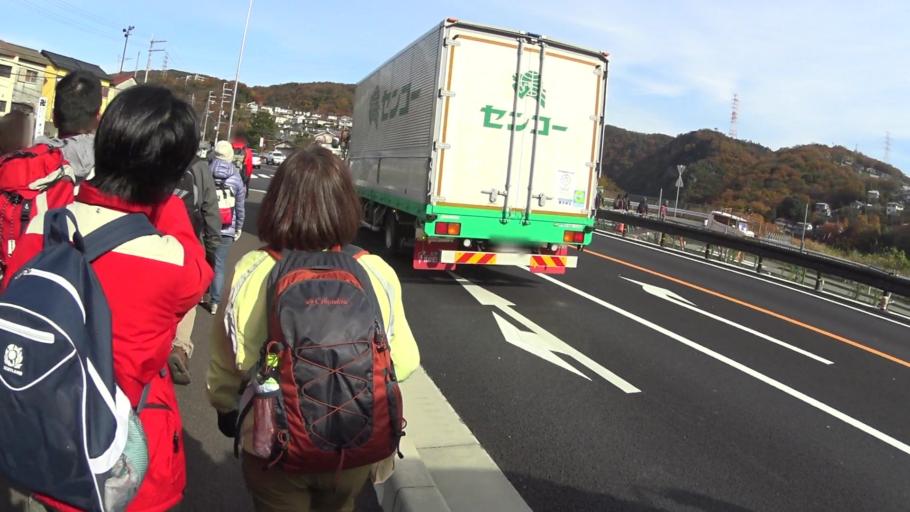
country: JP
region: Hyogo
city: Takarazuka
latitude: 34.8243
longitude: 135.3182
